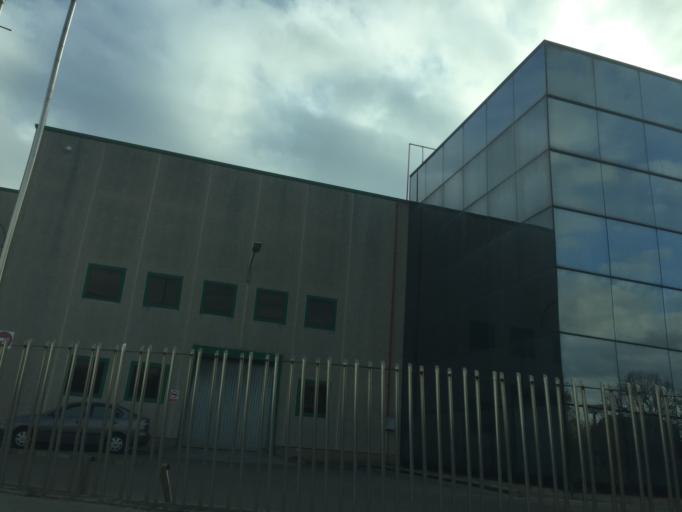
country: ES
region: Catalonia
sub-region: Provincia de Barcelona
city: El Prat de Llobregat
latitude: 41.3305
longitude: 2.0853
